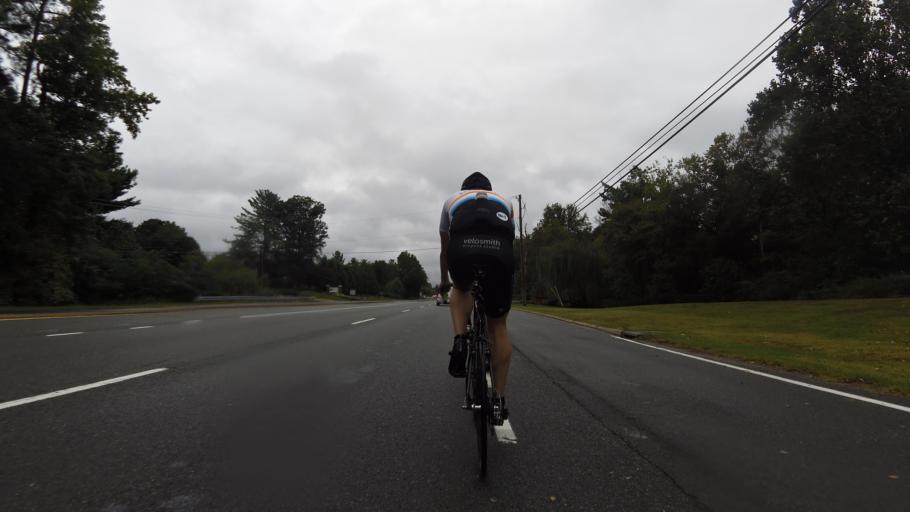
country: US
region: Virginia
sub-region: Henrico County
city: Tuckahoe
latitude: 37.5966
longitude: -77.5994
